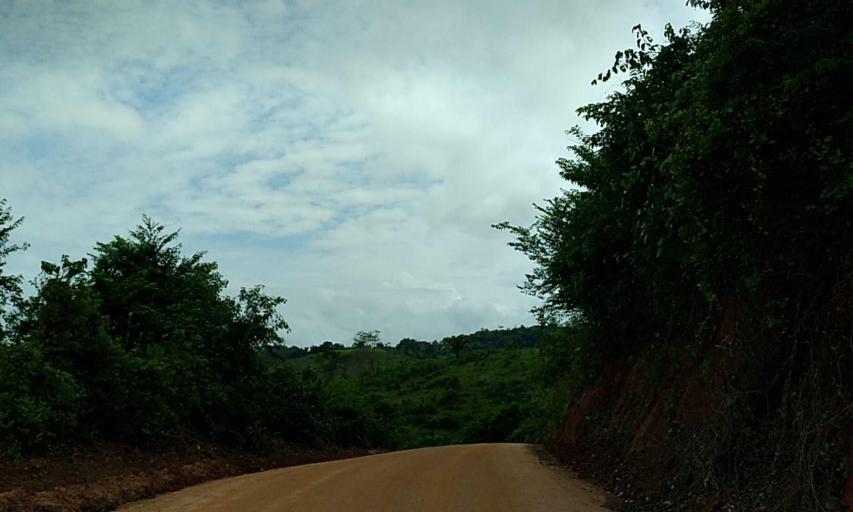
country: BR
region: Para
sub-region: Altamira
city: Altamira
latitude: -3.0809
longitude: -51.6347
